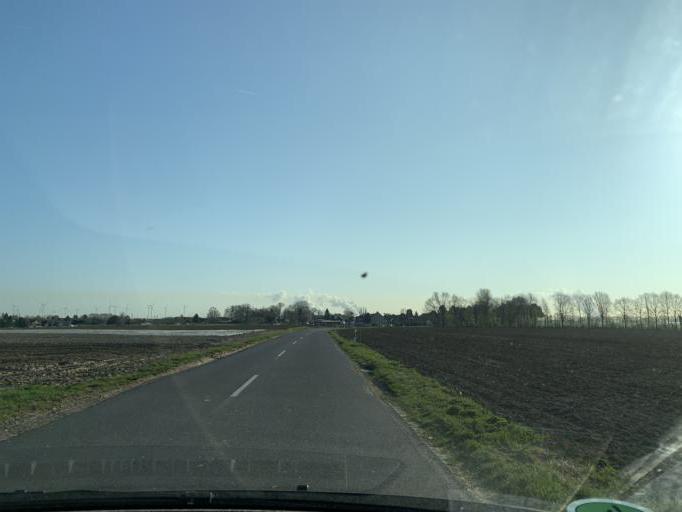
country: DE
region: North Rhine-Westphalia
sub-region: Regierungsbezirk Koln
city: Titz
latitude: 50.9936
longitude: 6.4809
